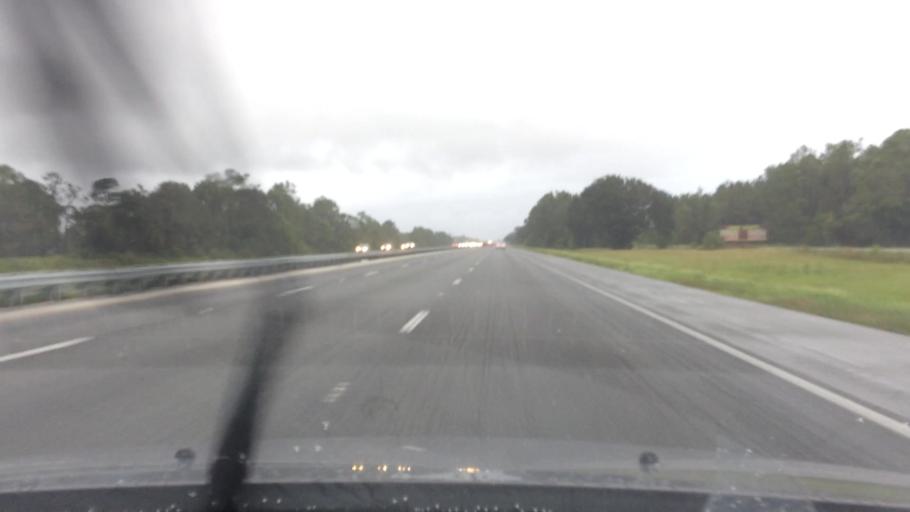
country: US
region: Florida
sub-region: Volusia County
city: Ormond-by-the-Sea
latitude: 29.3065
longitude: -81.1316
